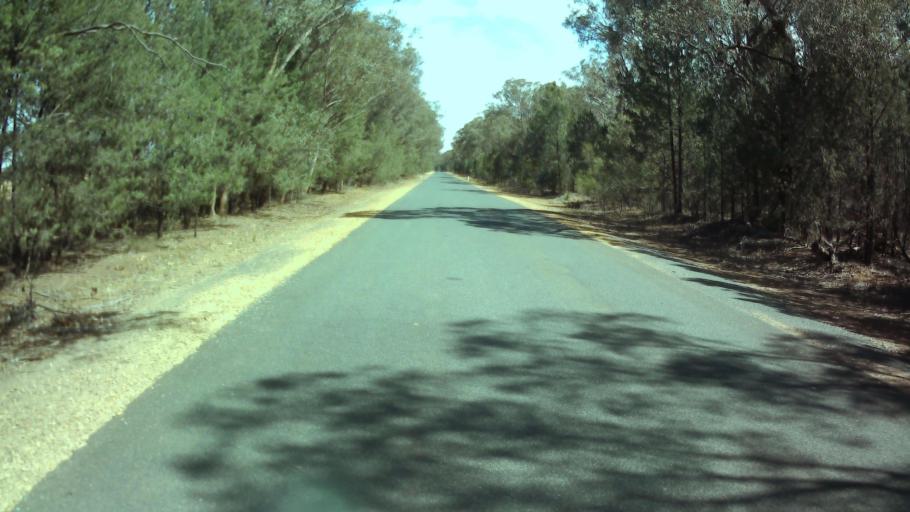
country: AU
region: New South Wales
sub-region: Weddin
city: Grenfell
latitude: -34.0160
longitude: 148.1291
